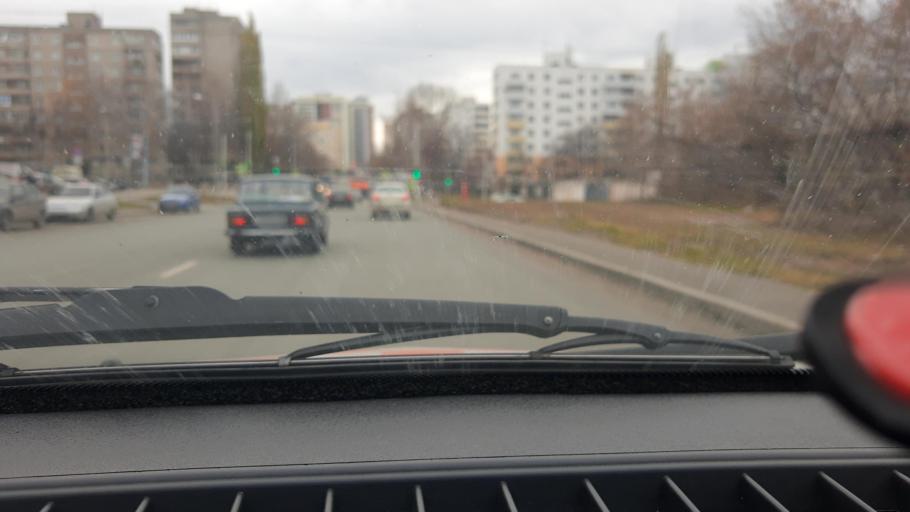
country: RU
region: Bashkortostan
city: Ufa
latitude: 54.7213
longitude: 55.9999
